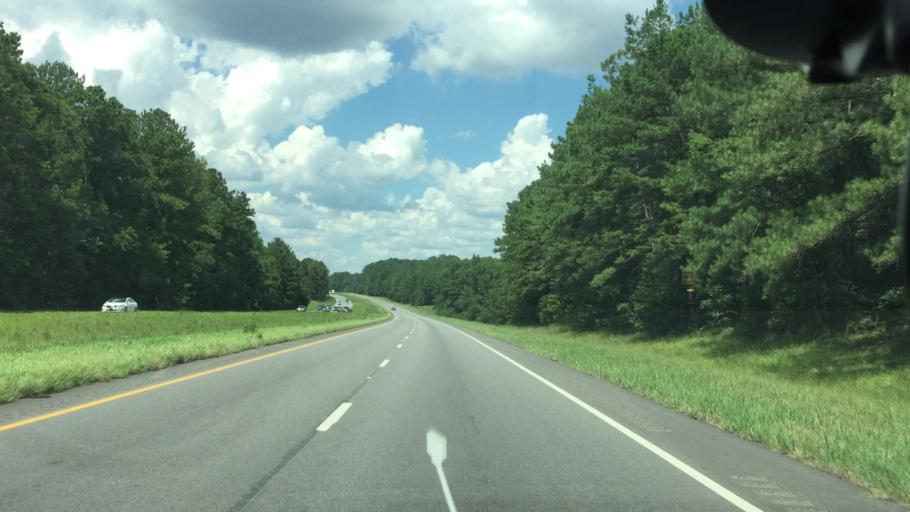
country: US
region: Alabama
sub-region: Pike County
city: Troy
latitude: 31.9067
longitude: -86.0115
